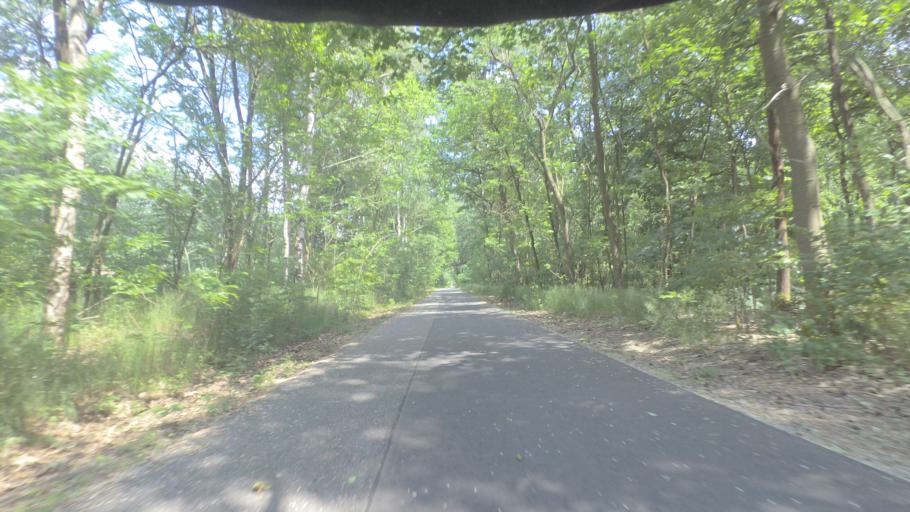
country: DE
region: Brandenburg
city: Fichtenwalde
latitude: 52.2580
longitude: 12.9187
